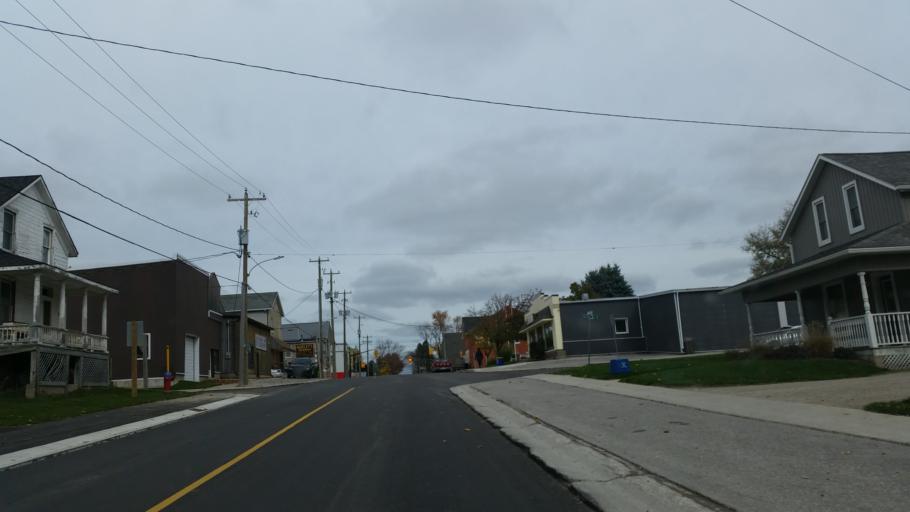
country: CA
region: Ontario
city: Hanover
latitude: 44.0414
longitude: -81.1200
